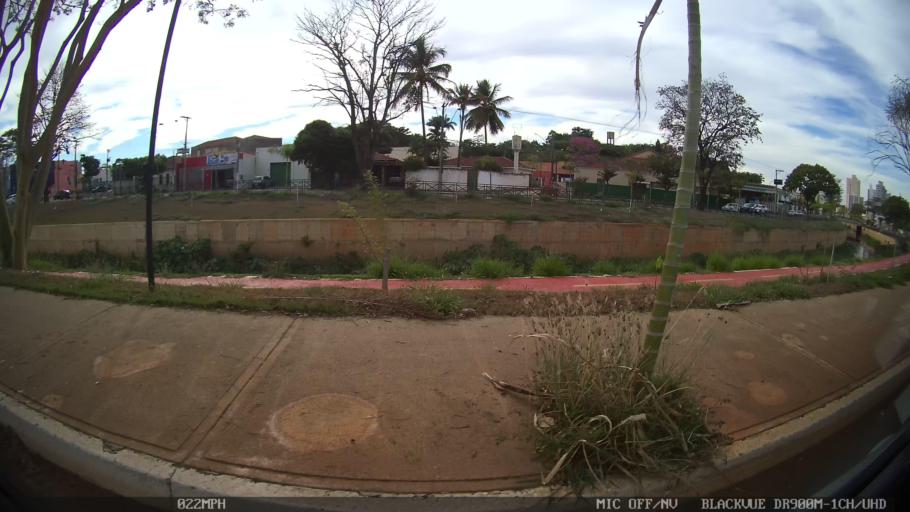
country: BR
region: Sao Paulo
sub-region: Catanduva
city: Catanduva
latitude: -21.1298
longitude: -48.9794
